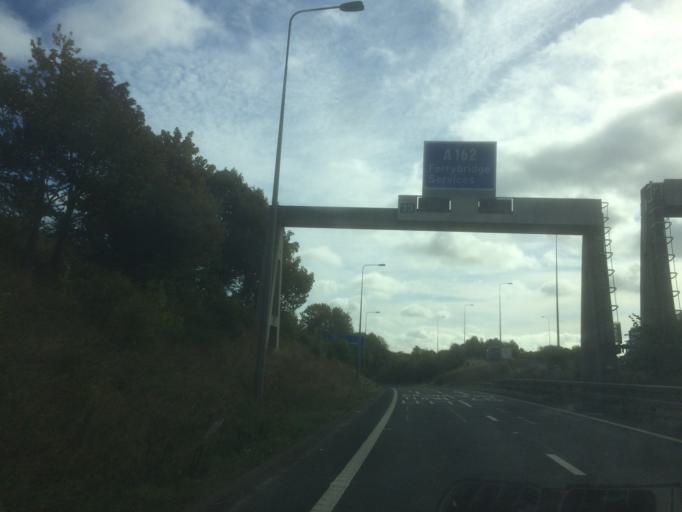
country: GB
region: England
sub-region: City and Borough of Wakefield
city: Ferrybridge
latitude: 53.6977
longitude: -1.2732
